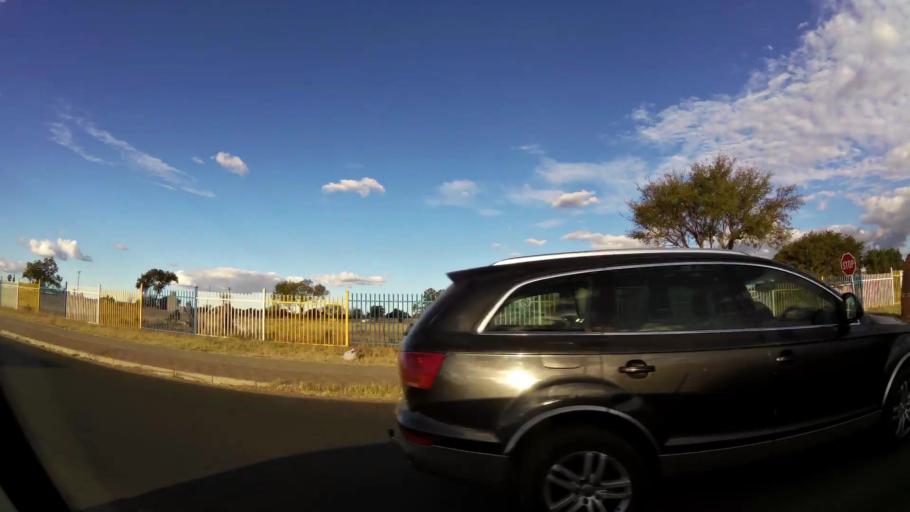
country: ZA
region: Limpopo
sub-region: Capricorn District Municipality
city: Polokwane
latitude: -23.9071
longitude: 29.4293
